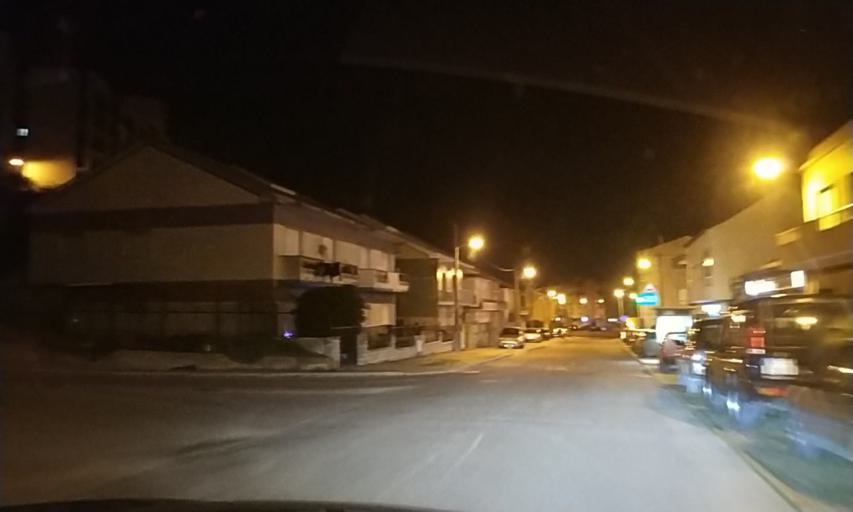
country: PT
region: Setubal
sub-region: Setubal
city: Setubal
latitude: 38.5259
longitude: -8.9081
